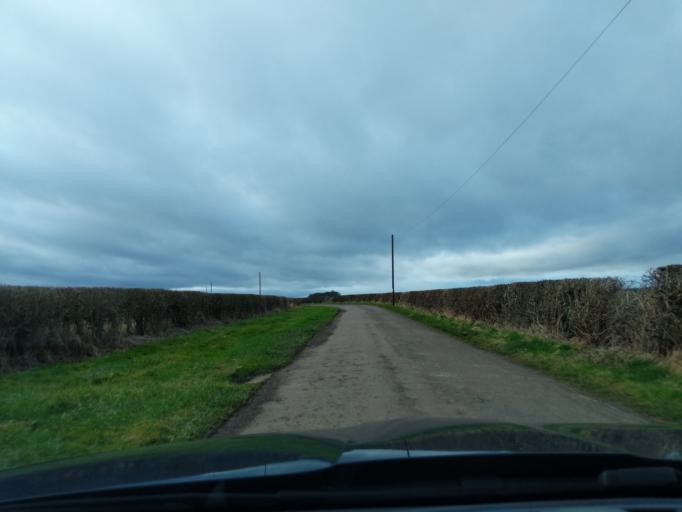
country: GB
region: England
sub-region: Northumberland
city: Ancroft
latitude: 55.6959
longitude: -1.9815
